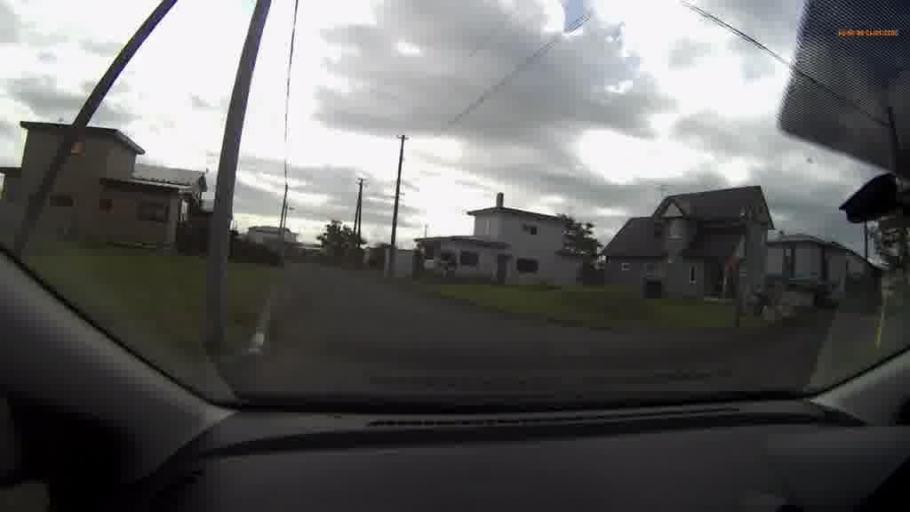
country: JP
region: Hokkaido
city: Kushiro
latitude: 42.9758
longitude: 144.1285
